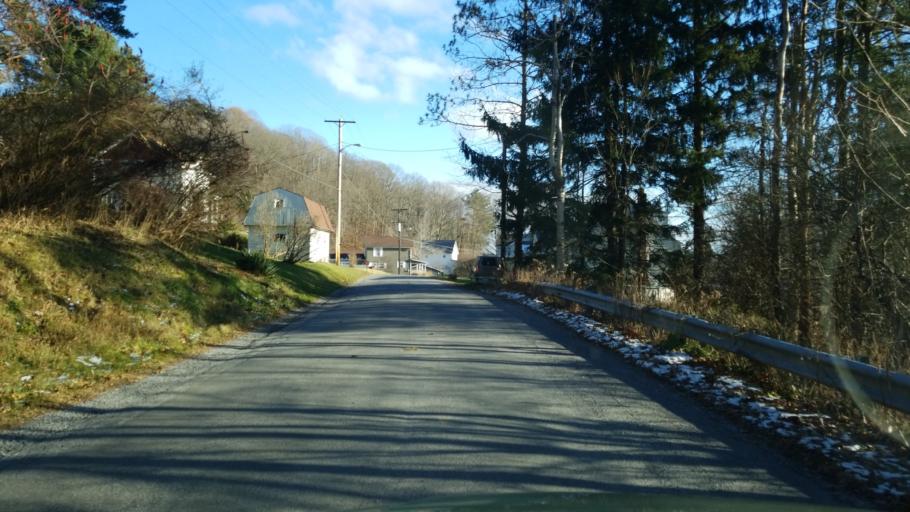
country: US
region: Pennsylvania
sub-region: Jefferson County
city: Brockway
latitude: 41.2557
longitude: -78.7971
